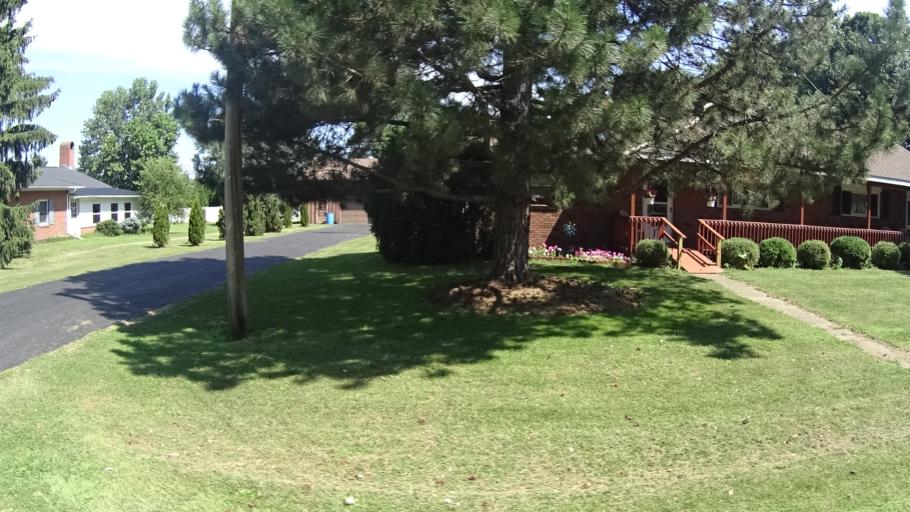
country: US
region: Ohio
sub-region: Erie County
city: Sandusky
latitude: 41.4275
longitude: -82.7731
